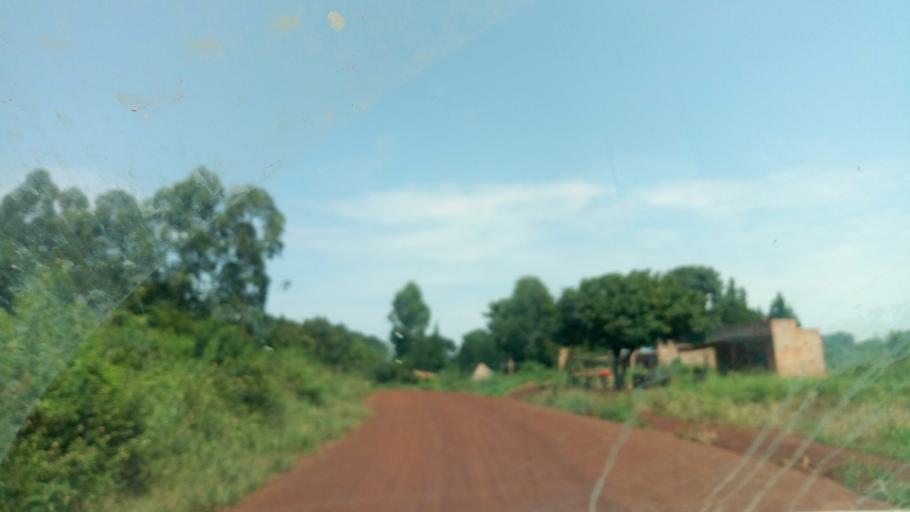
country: UG
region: Western Region
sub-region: Masindi District
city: Masindi
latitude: 1.6701
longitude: 31.8243
